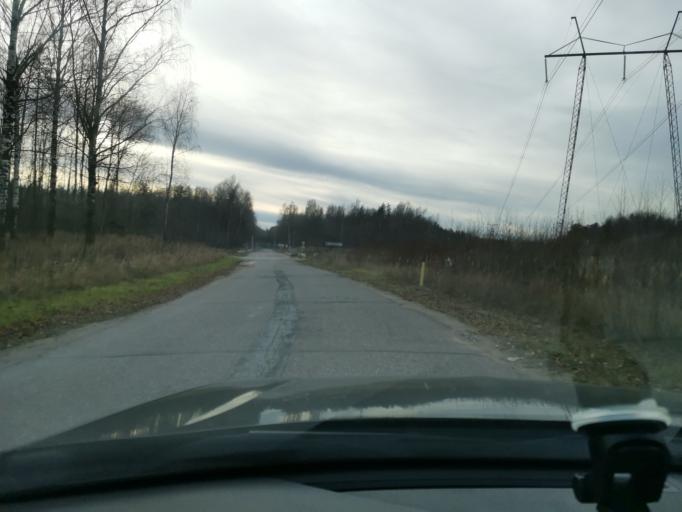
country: EE
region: Ida-Virumaa
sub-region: Sillamaee linn
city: Sillamae
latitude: 59.2661
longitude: 27.8995
